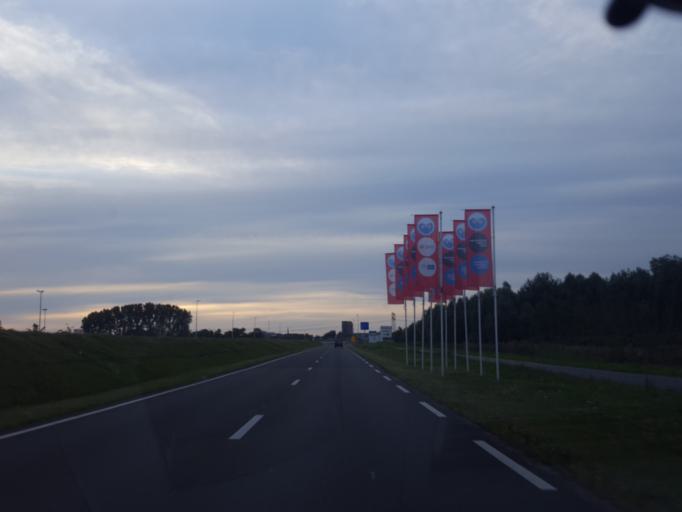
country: NL
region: Friesland
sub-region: Gemeente Leeuwarden
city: Huizum
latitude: 53.1756
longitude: 5.8245
